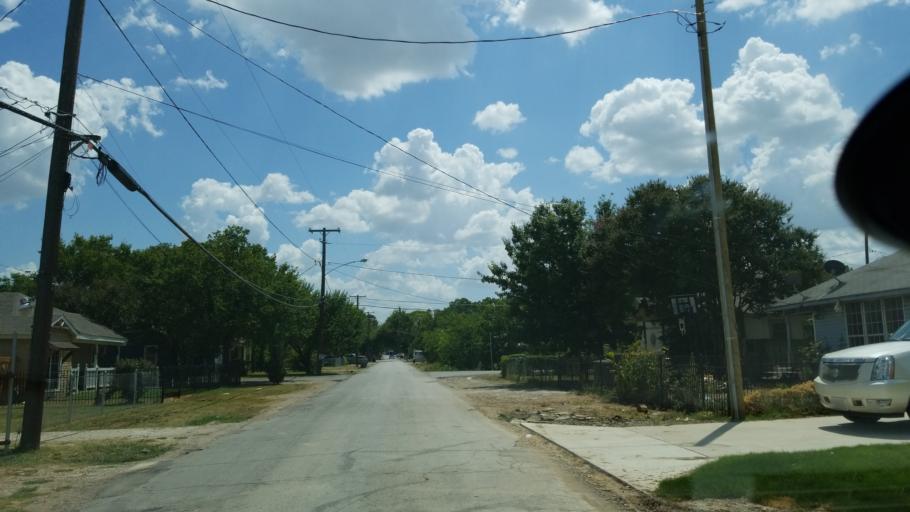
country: US
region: Texas
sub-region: Dallas County
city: Cockrell Hill
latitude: 32.7486
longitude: -96.9076
